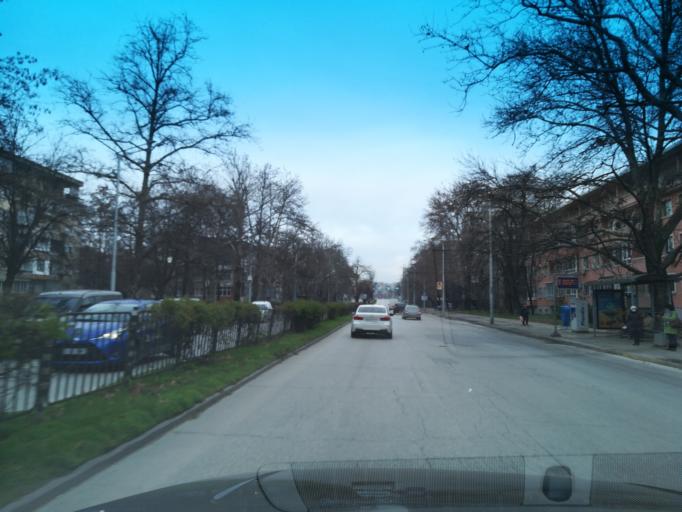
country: BG
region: Plovdiv
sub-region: Obshtina Plovdiv
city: Plovdiv
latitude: 42.1487
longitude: 24.7312
